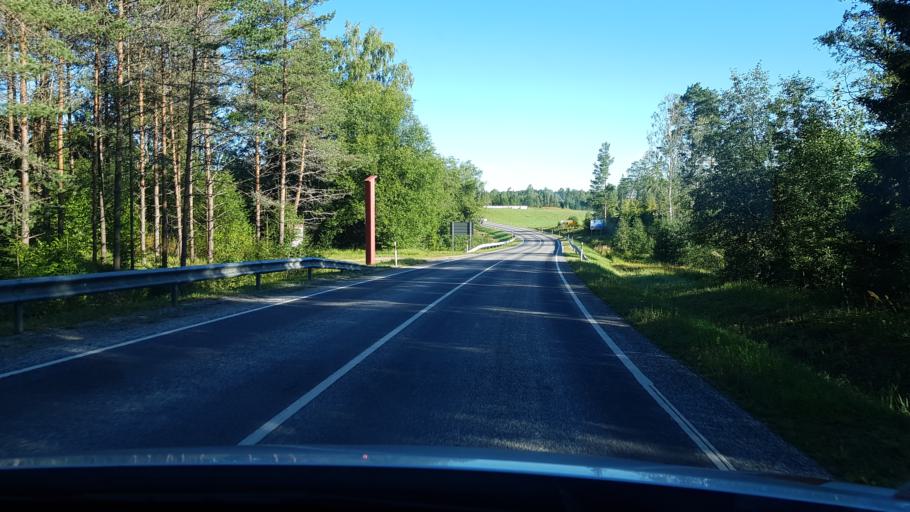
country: EE
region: Vorumaa
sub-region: Antsla vald
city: Vana-Antsla
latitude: 58.0189
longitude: 26.5867
